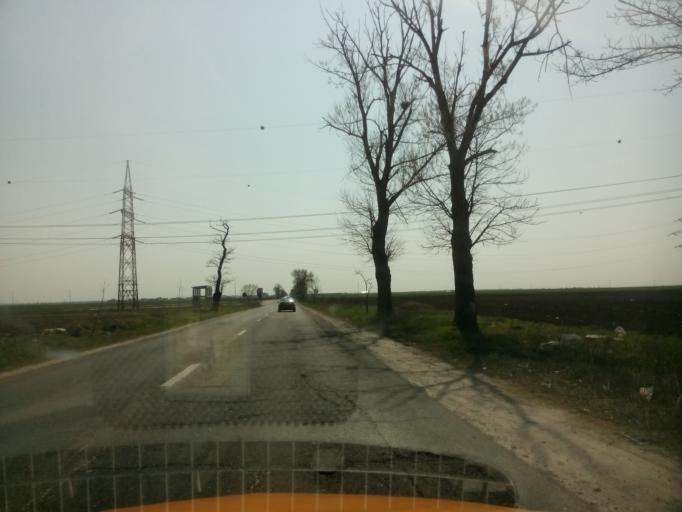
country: RO
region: Ilfov
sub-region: Comuna Glina
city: Glina
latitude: 44.3503
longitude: 26.2171
